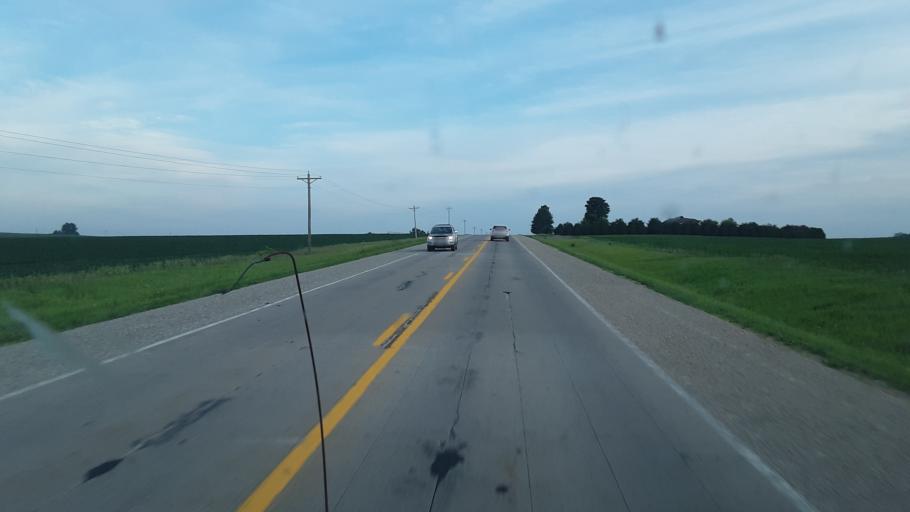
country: US
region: Iowa
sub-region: Benton County
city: Belle Plaine
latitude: 41.8051
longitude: -92.2789
